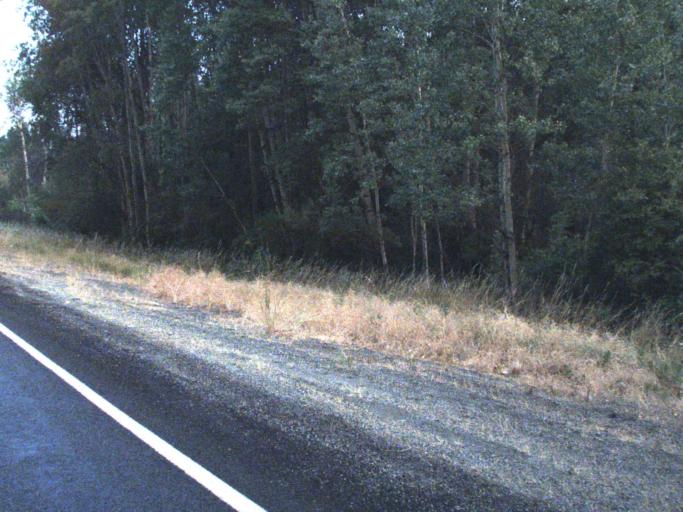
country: US
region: Washington
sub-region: Kittitas County
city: Cle Elum
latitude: 47.1717
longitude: -120.8452
